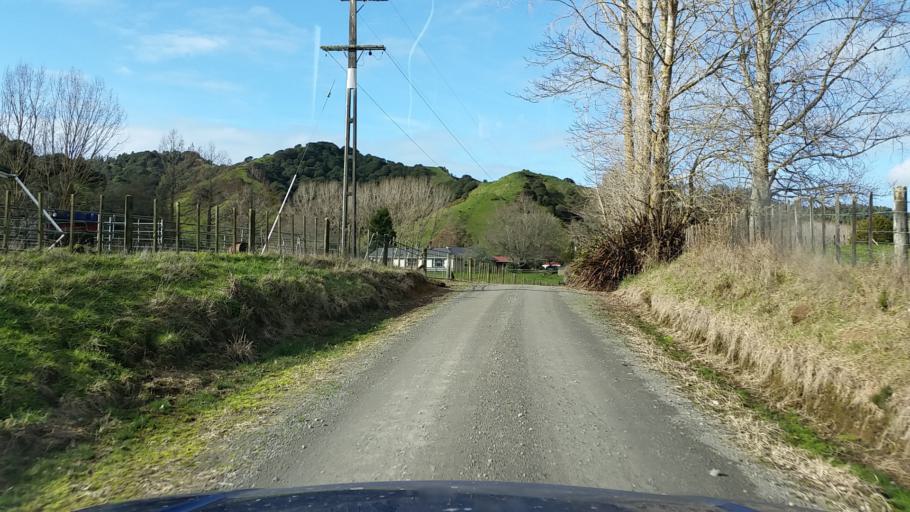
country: NZ
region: Taranaki
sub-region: South Taranaki District
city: Eltham
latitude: -39.2596
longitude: 174.5896
